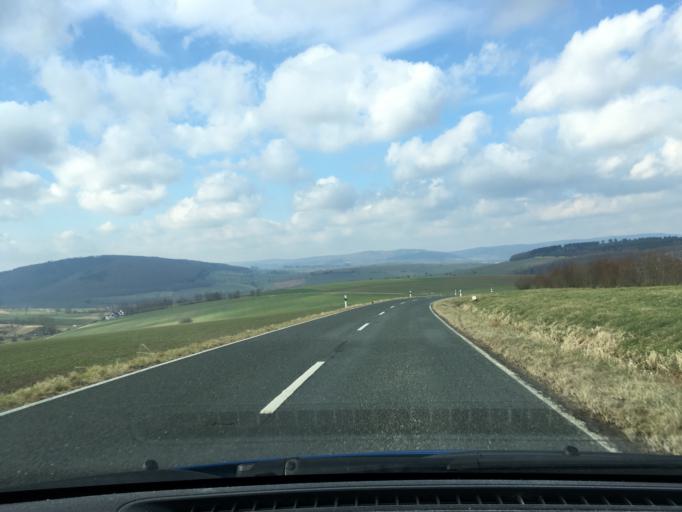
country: DE
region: Lower Saxony
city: Uslar
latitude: 51.6104
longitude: 9.6313
